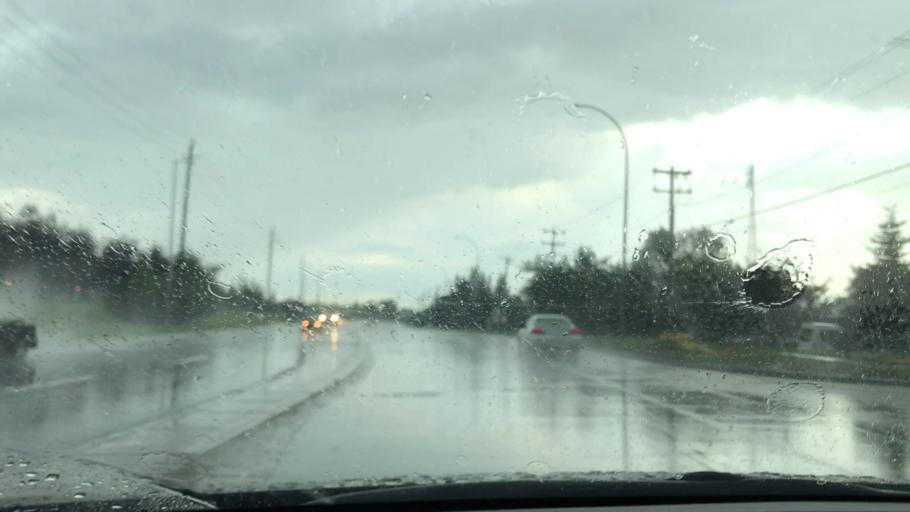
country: CA
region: Alberta
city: Edmonton
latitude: 53.4915
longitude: -113.4460
